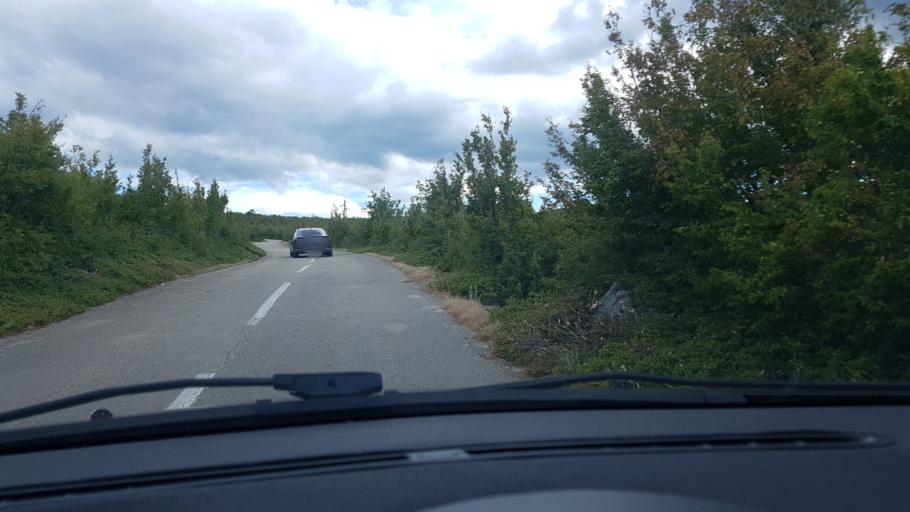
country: HR
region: Zadarska
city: Gracac
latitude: 44.1870
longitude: 15.8881
